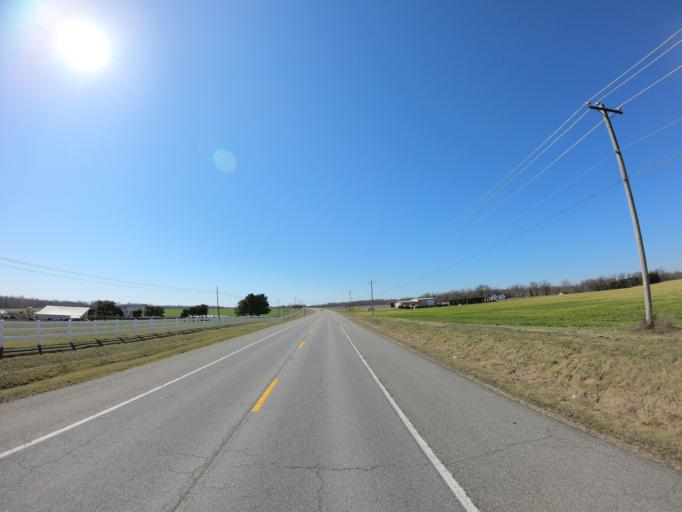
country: US
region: Maryland
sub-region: Queen Anne's County
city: Kingstown
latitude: 39.2918
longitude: -76.0101
